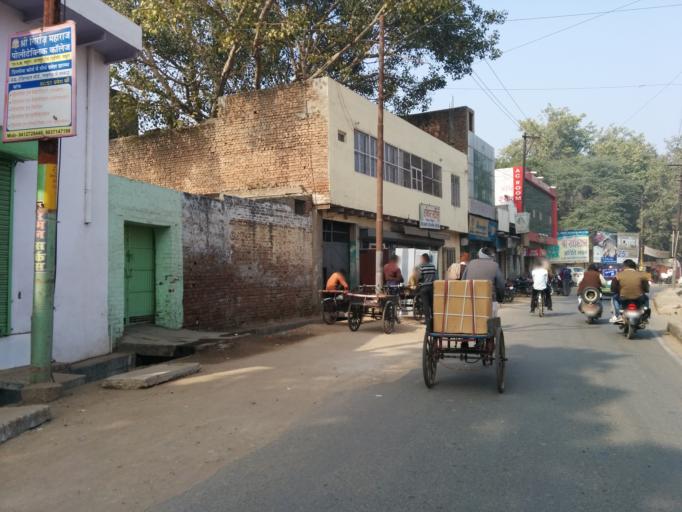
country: IN
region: Uttar Pradesh
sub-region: Mathura
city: Mathura
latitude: 27.5099
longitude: 77.6716
